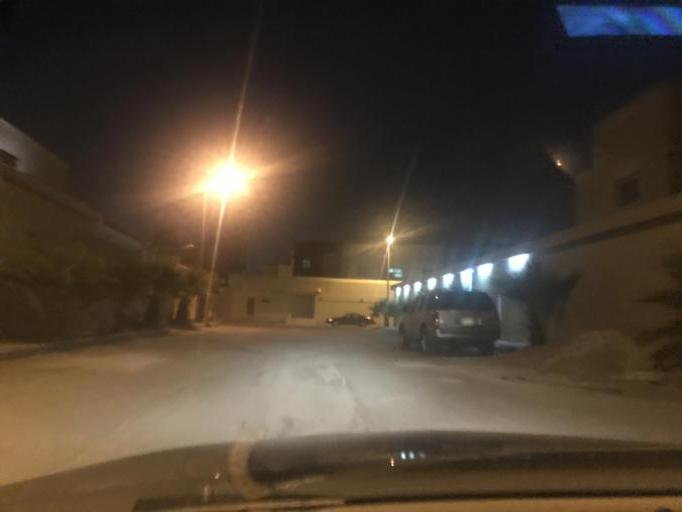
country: SA
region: Ar Riyad
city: Riyadh
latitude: 24.7494
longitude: 46.7517
